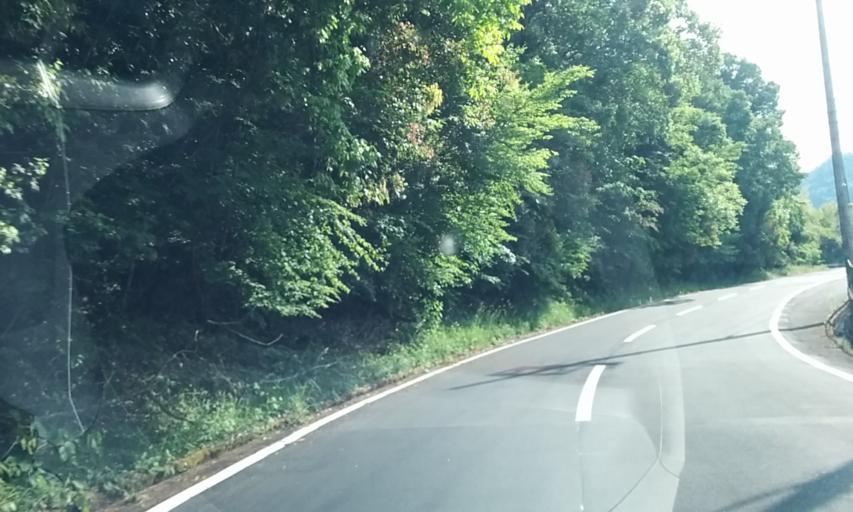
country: JP
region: Kyoto
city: Ayabe
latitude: 35.3340
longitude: 135.2973
